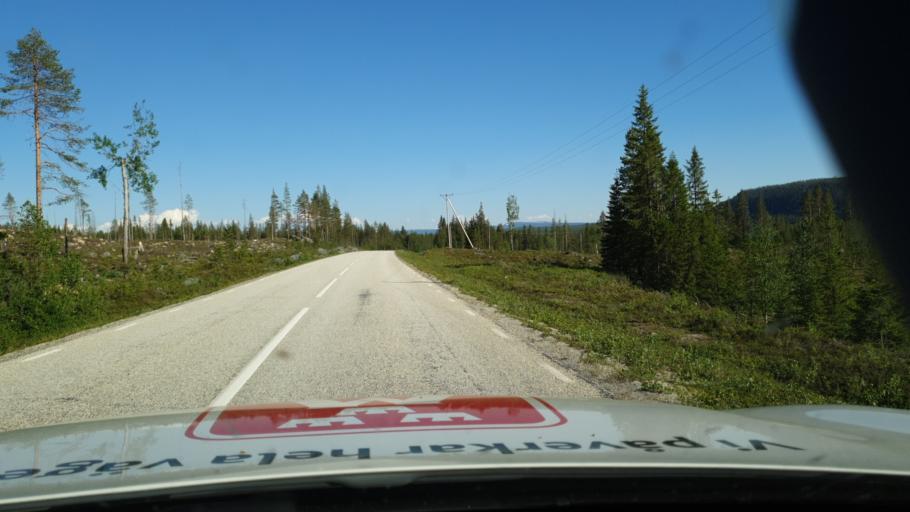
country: SE
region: Jaemtland
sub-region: Are Kommun
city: Jarpen
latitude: 62.7679
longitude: 13.7227
